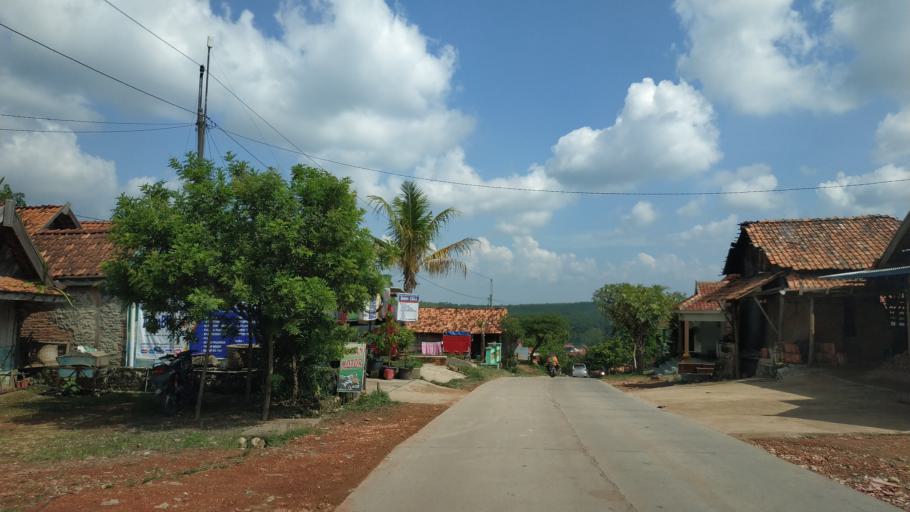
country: ID
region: Central Java
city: Jepang
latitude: -7.0111
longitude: 111.1177
